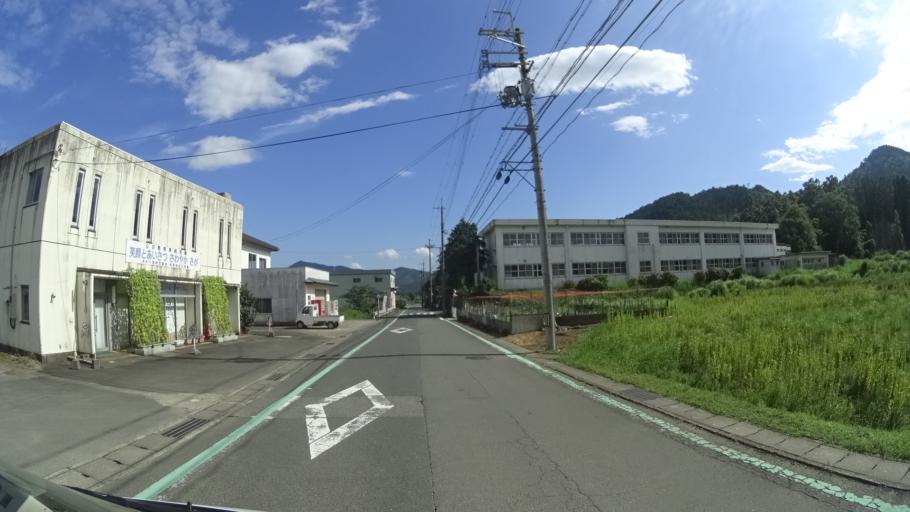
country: JP
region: Kyoto
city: Fukuchiyama
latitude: 35.3207
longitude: 135.1810
